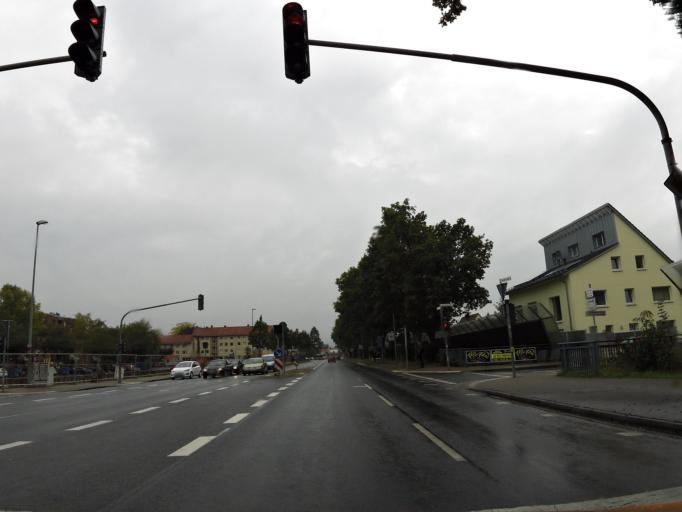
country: DE
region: Lower Saxony
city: Goettingen
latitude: 51.5563
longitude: 9.9394
